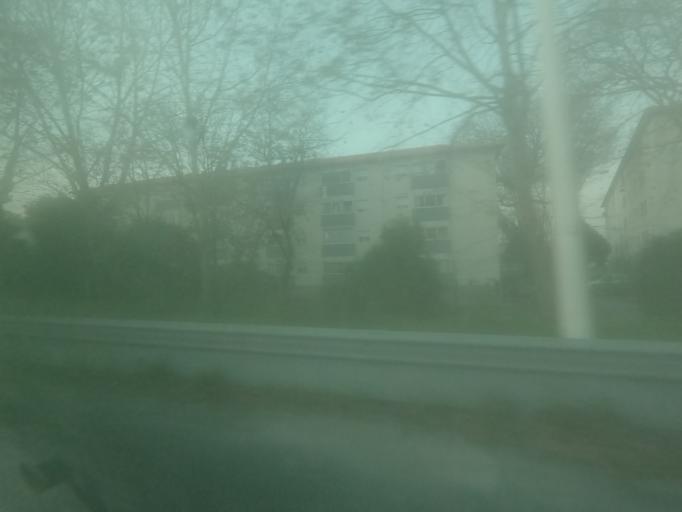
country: PT
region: Porto
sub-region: Porto
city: Porto
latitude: 41.1741
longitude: -8.6180
